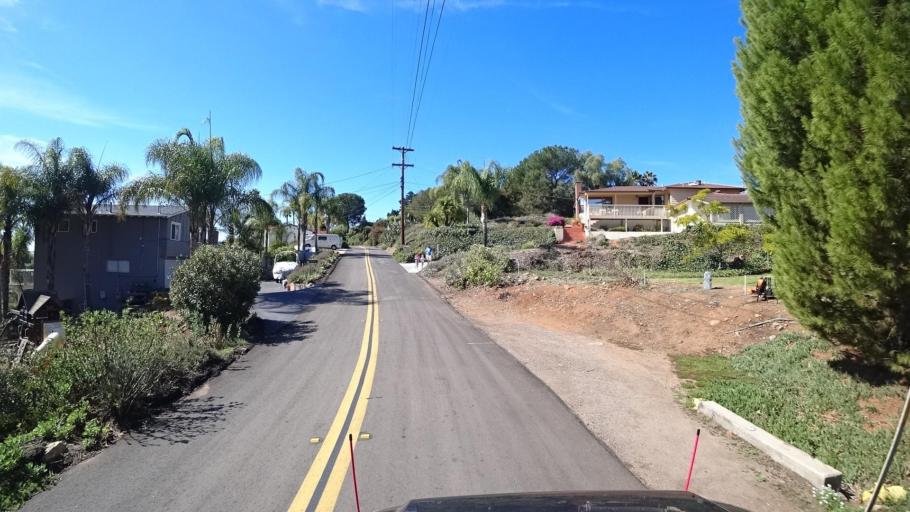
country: US
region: California
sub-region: San Diego County
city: Casa de Oro-Mount Helix
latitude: 32.7618
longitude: -116.9634
